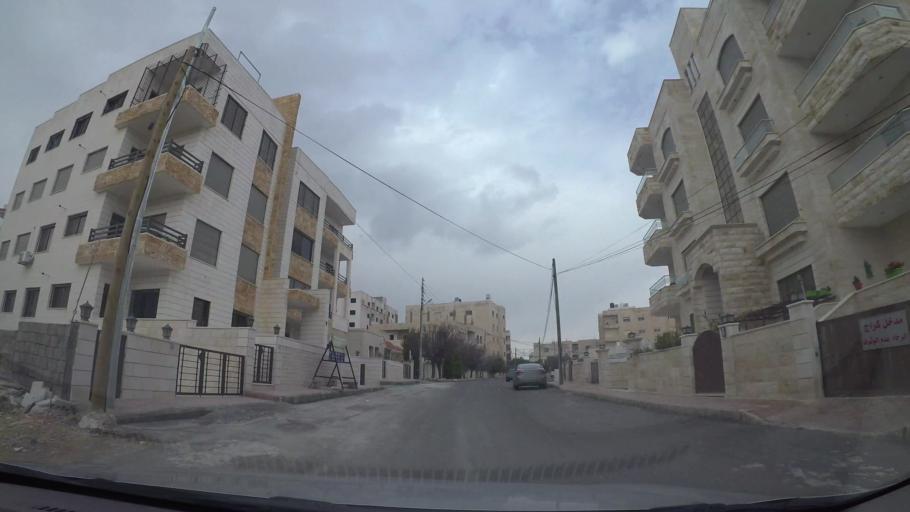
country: JO
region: Amman
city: Umm as Summaq
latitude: 31.9056
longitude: 35.8502
